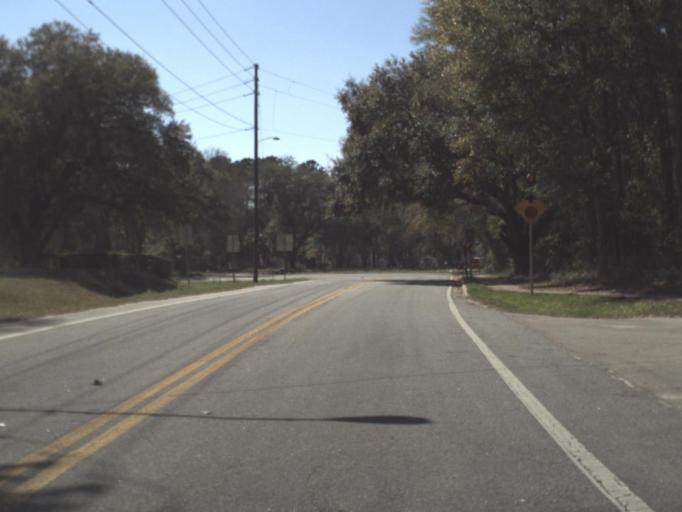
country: US
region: Florida
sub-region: Leon County
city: Tallahassee
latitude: 30.4132
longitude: -84.3081
